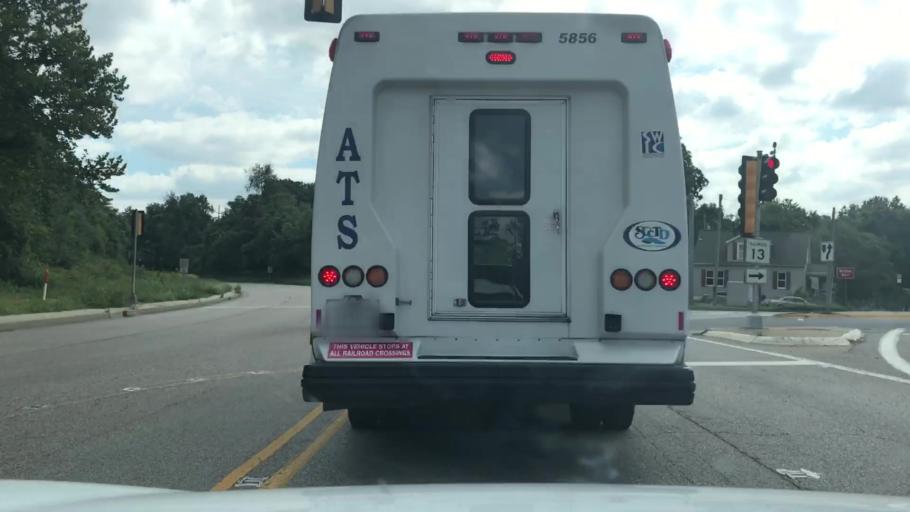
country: US
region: Illinois
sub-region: Saint Clair County
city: Swansea
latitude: 38.5424
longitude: -90.0480
